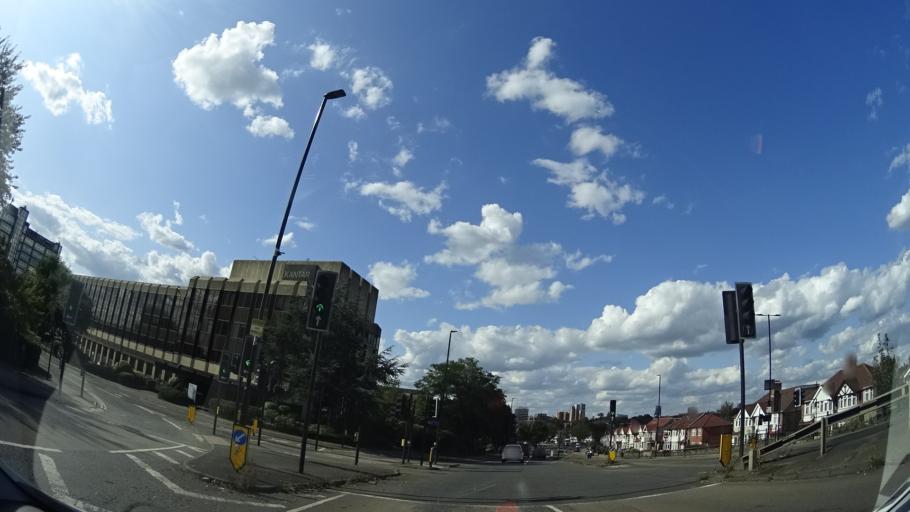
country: GB
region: England
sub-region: Greater London
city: Ealing Broadway
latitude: 51.5317
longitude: -0.2949
